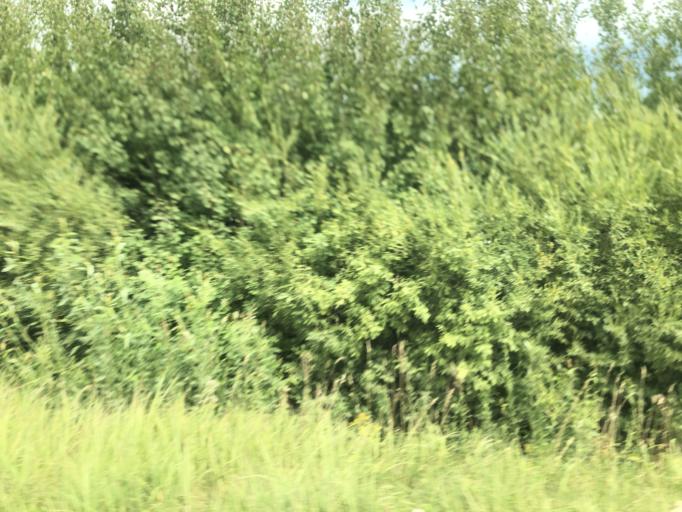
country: LV
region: Vecumnieki
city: Vecumnieki
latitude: 56.4586
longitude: 24.6313
